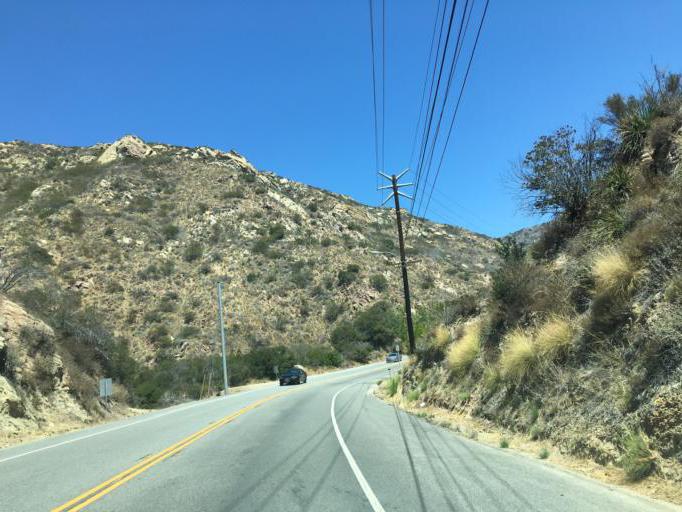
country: US
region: California
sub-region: Los Angeles County
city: Malibu Beach
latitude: 34.0535
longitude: -118.6965
